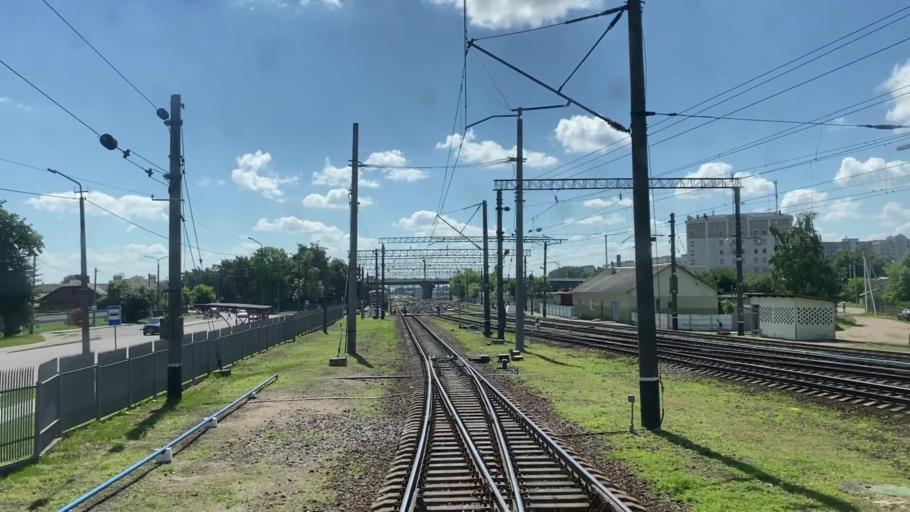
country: BY
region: Brest
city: Baranovichi
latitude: 53.1354
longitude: 26.0355
